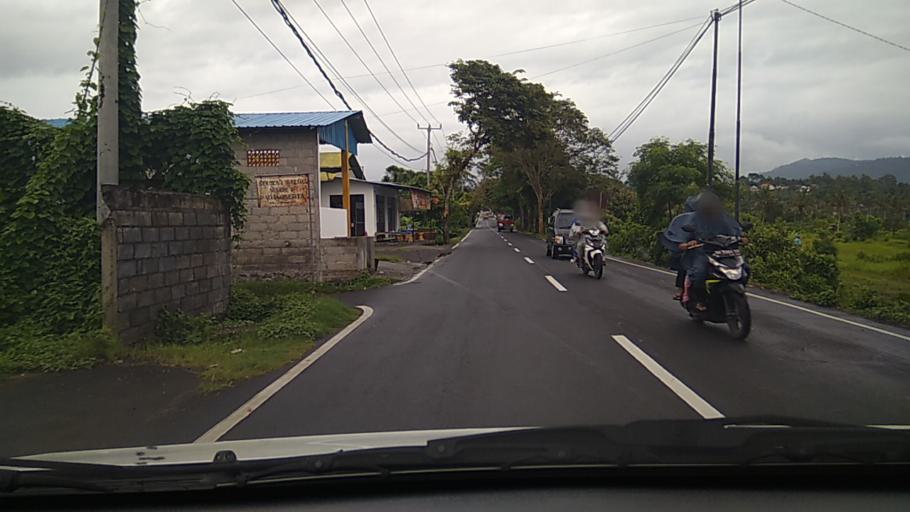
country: ID
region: Bali
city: Banjar Budakeling
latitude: -8.4306
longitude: 115.5916
